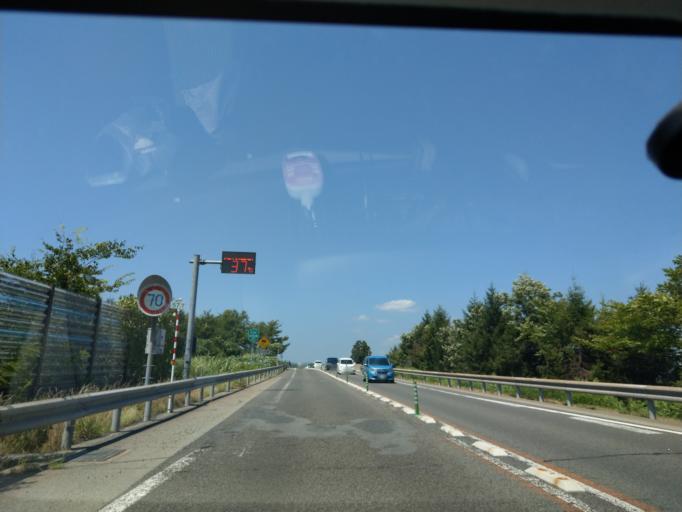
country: JP
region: Akita
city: Yokotemachi
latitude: 39.3307
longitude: 140.5085
